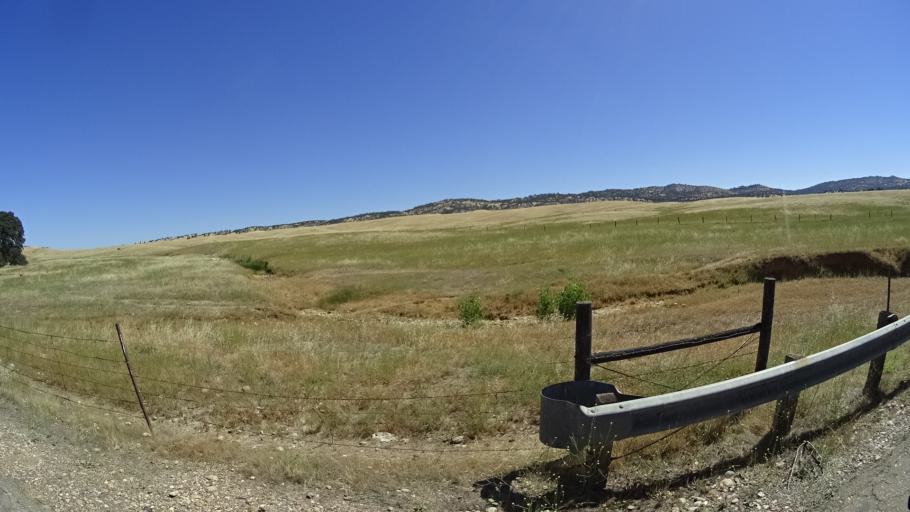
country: US
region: California
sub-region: Calaveras County
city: Rancho Calaveras
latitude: 38.0209
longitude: -120.8352
